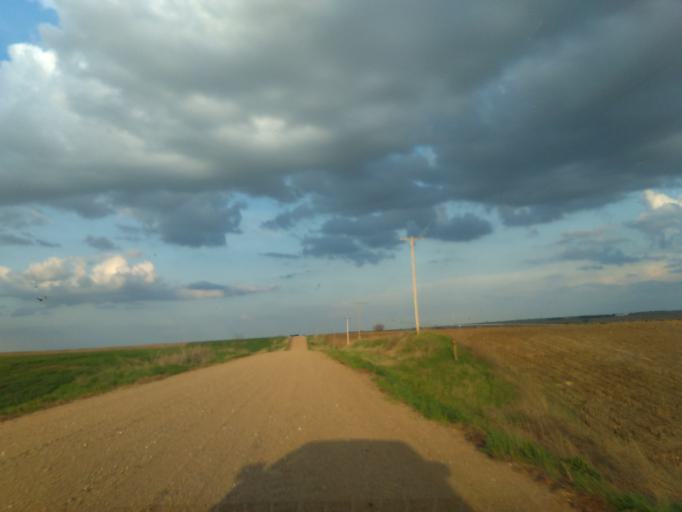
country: US
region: Nebraska
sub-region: Webster County
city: Red Cloud
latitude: 40.1763
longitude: -98.4219
